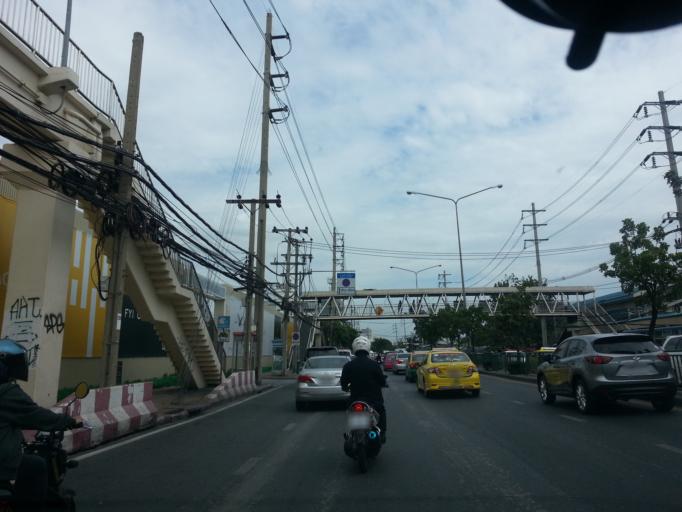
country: TH
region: Bangkok
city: Khlong Toei
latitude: 13.7202
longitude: 100.5594
